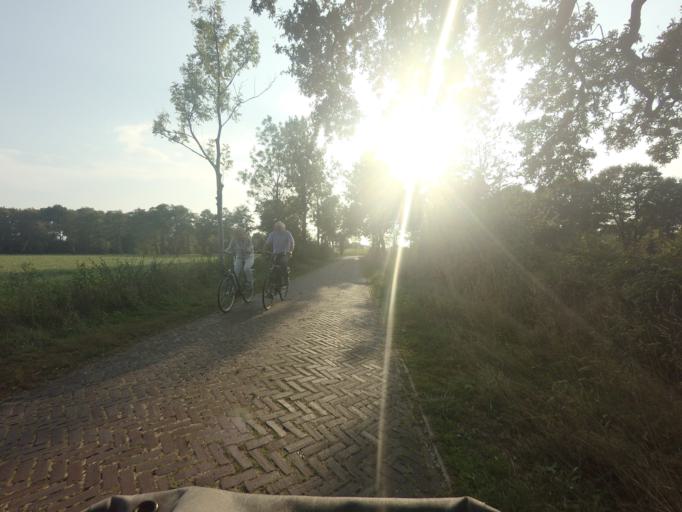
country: NL
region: Drenthe
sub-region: Gemeente Tynaarlo
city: Vries
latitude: 53.1268
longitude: 6.5523
